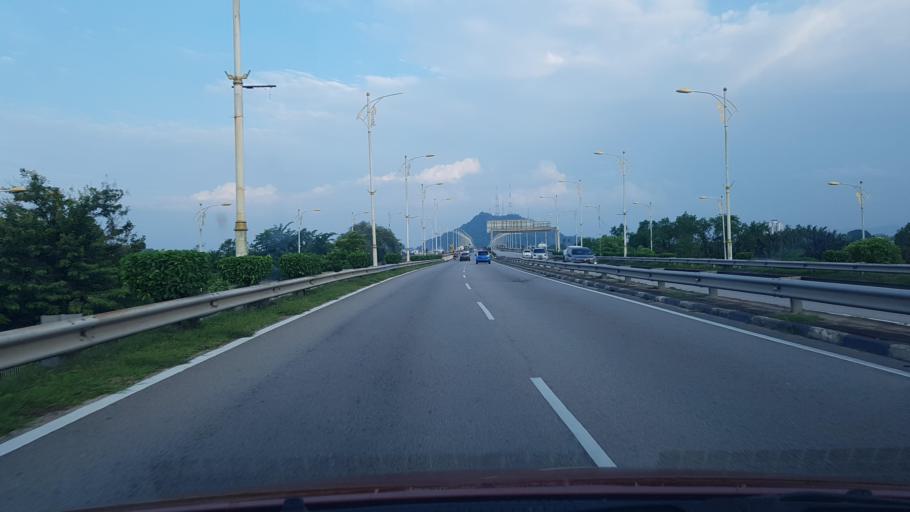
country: MY
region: Terengganu
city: Kuala Terengganu
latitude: 5.3286
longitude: 103.1227
